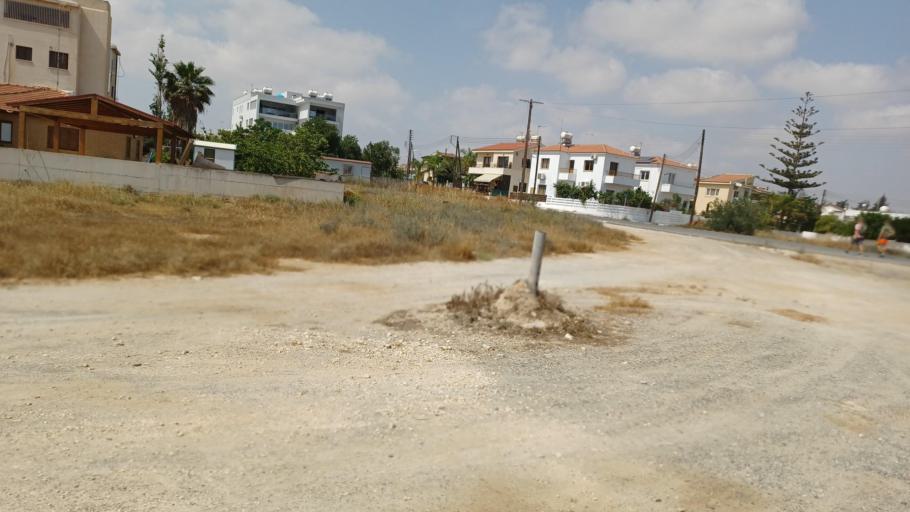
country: CY
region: Ammochostos
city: Deryneia
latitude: 35.0694
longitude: 33.9636
